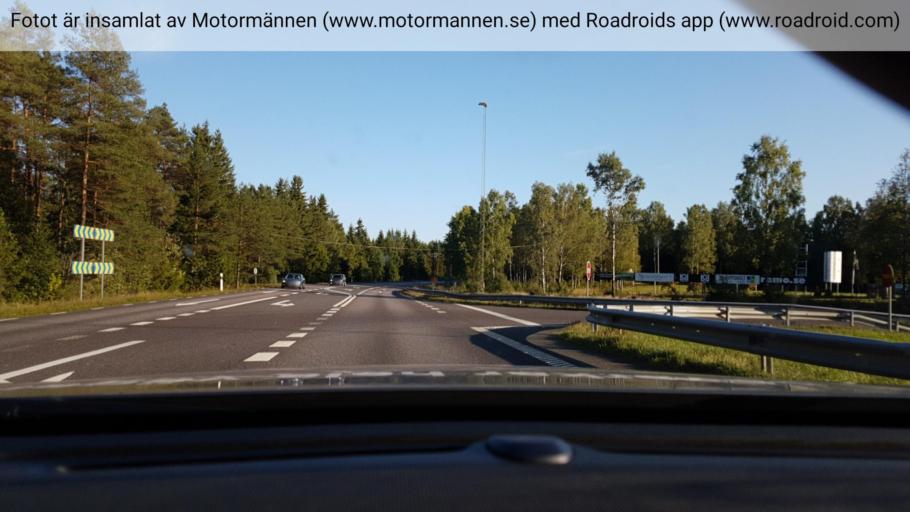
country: SE
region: Joenkoeping
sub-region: Gislaveds Kommun
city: Smalandsstenar
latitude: 57.1199
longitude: 13.3820
